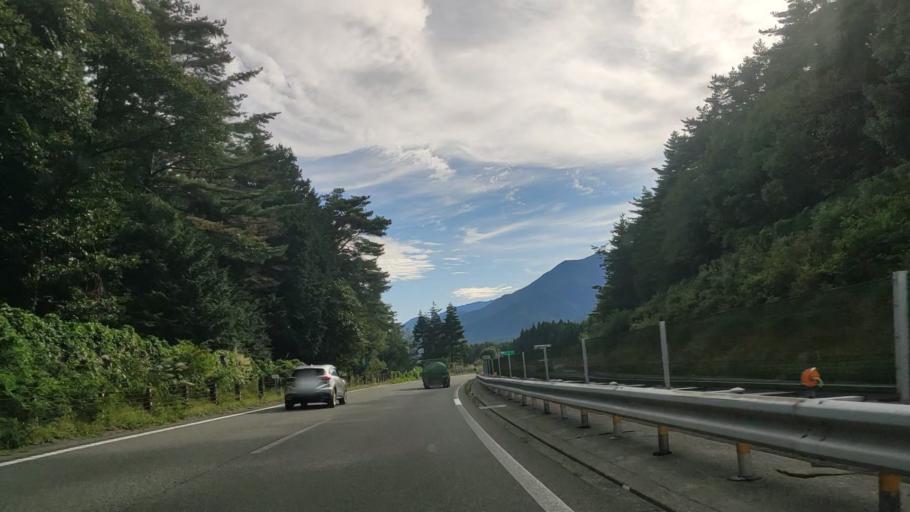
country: JP
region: Nagano
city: Ina
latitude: 35.7622
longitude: 137.9199
